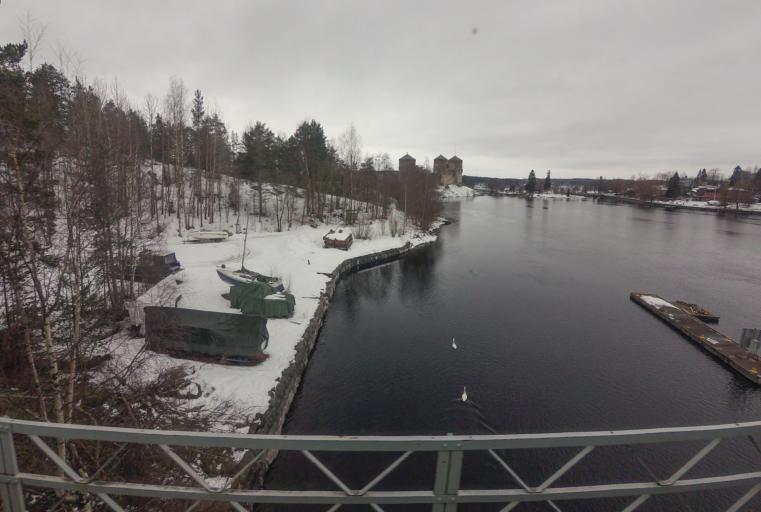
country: FI
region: Southern Savonia
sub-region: Savonlinna
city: Savonlinna
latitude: 61.8662
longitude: 28.9047
